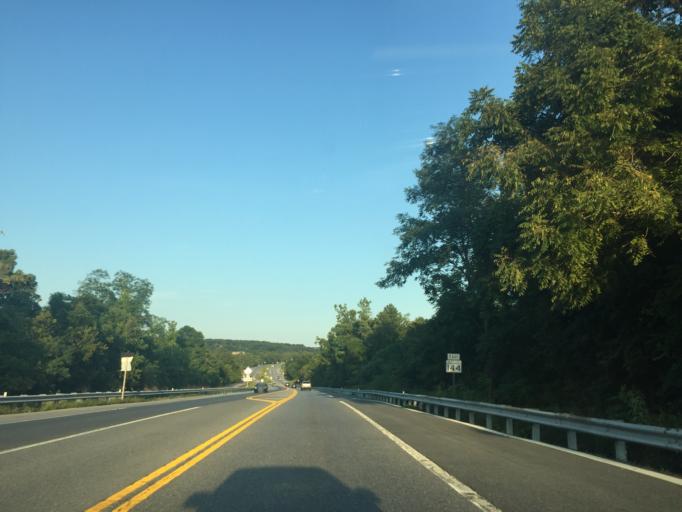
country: US
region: Maryland
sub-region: Frederick County
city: Bartonsville
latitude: 39.3968
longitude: -77.3604
